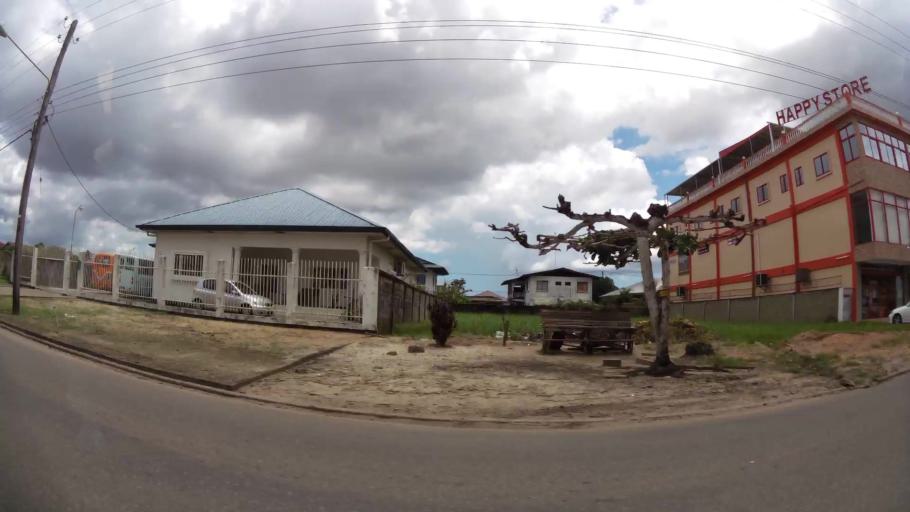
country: SR
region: Paramaribo
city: Paramaribo
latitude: 5.8571
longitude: -55.1352
